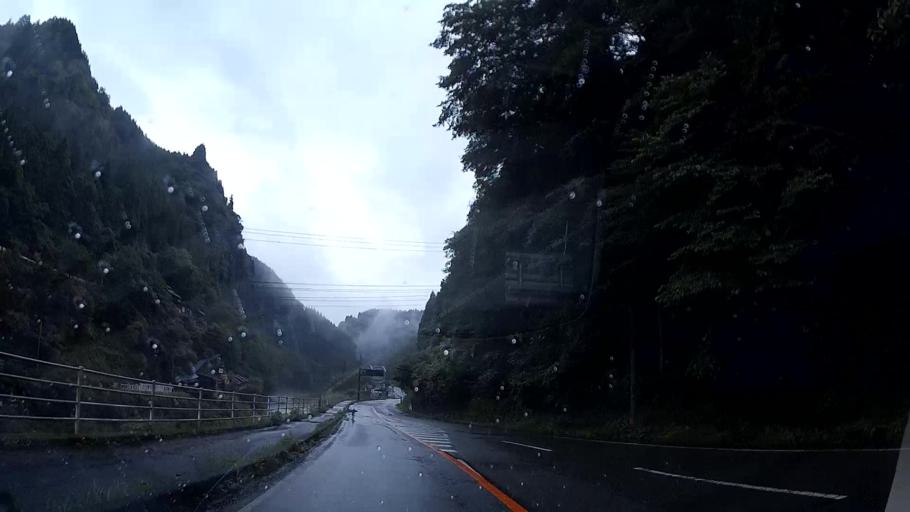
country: JP
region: Oita
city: Tsukawaki
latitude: 33.1747
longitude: 131.0365
